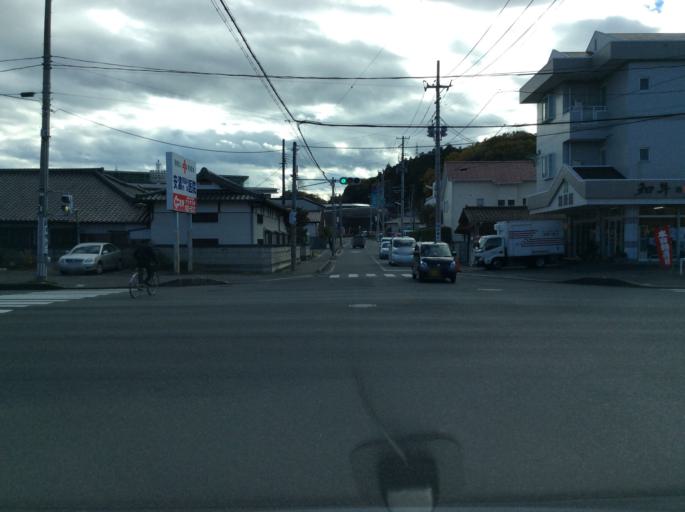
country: JP
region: Fukushima
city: Iwaki
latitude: 37.0480
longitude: 140.8903
